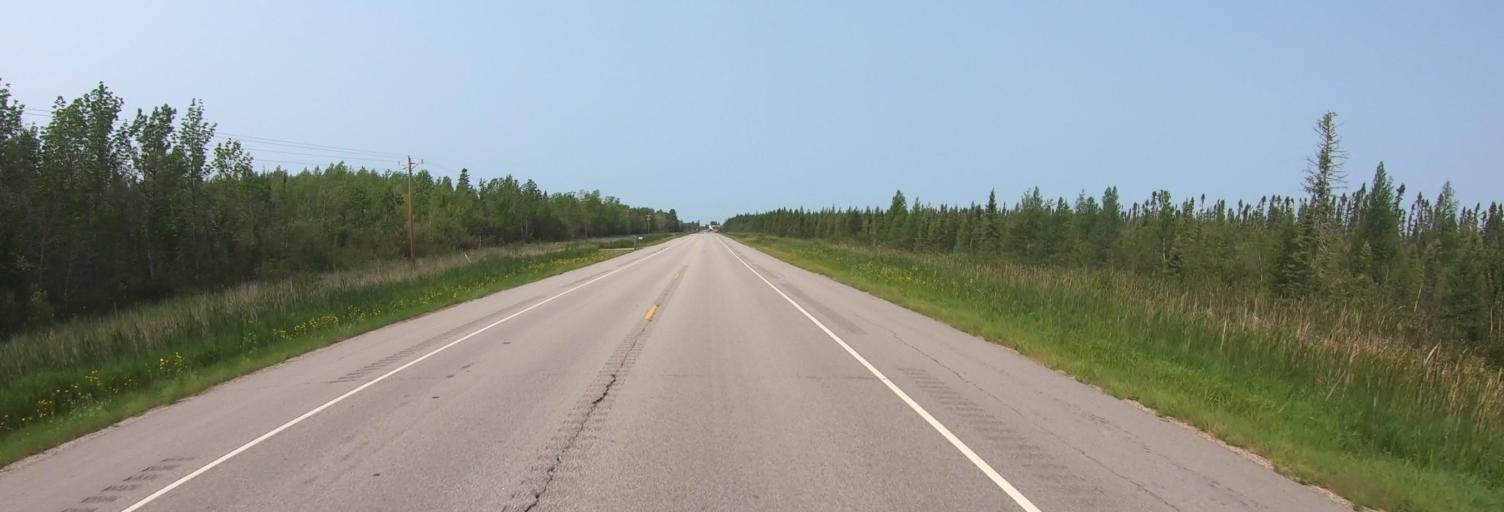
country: CA
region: Ontario
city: Fort Frances
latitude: 48.4105
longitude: -93.1839
